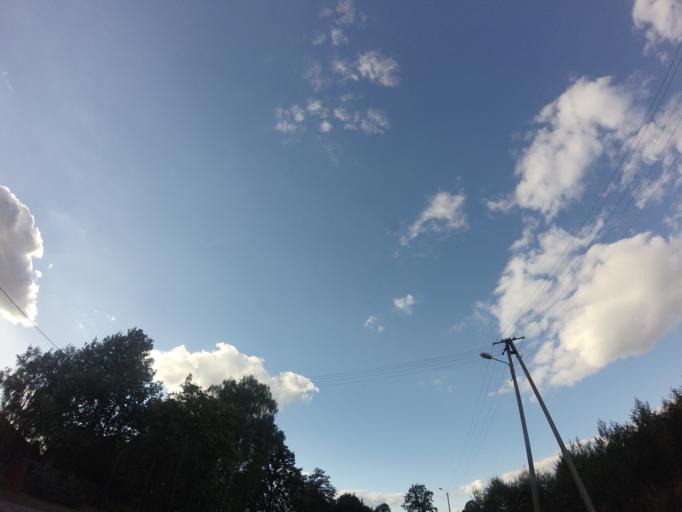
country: PL
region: Greater Poland Voivodeship
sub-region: Powiat nowotomyski
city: Nowy Tomysl
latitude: 52.2711
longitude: 16.1281
